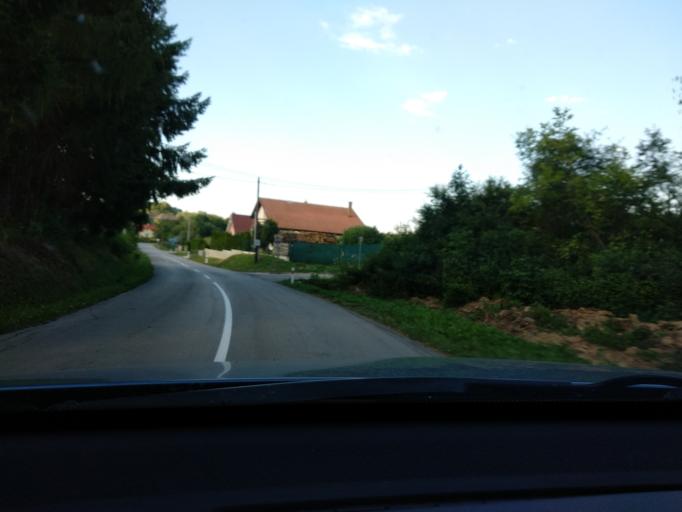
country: SK
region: Nitriansky
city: Banovce nad Bebravou
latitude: 48.7350
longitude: 18.1641
